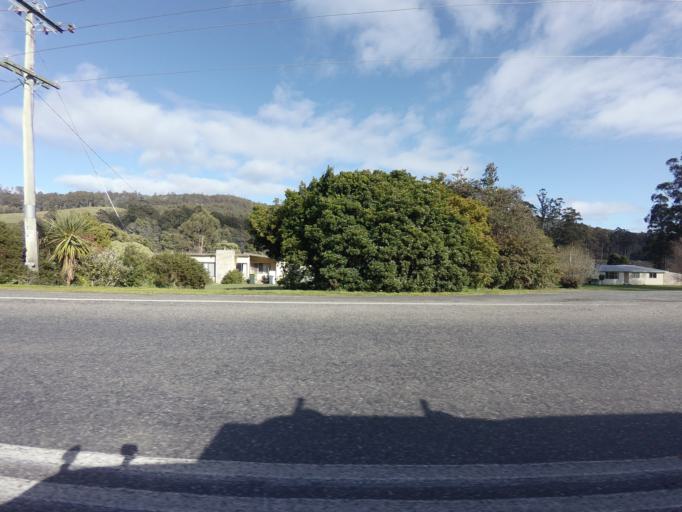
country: AU
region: Tasmania
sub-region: Huon Valley
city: Cygnet
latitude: -43.2886
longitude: 147.0106
